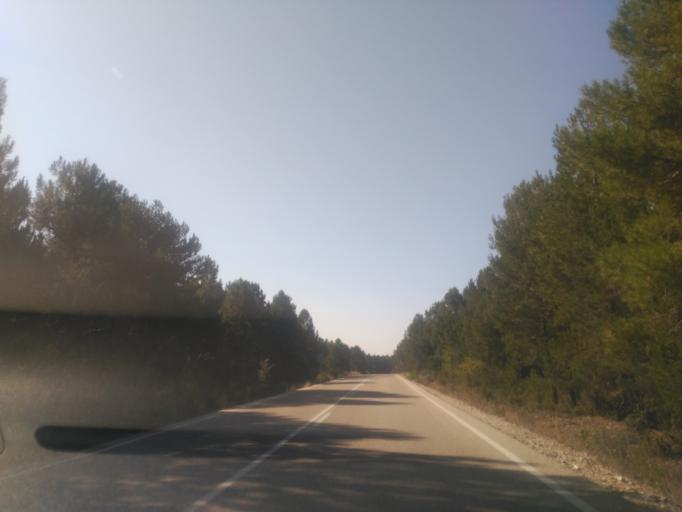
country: ES
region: Castille and Leon
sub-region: Provincia de Soria
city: Herrera de Soria
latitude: 41.7638
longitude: -3.0332
